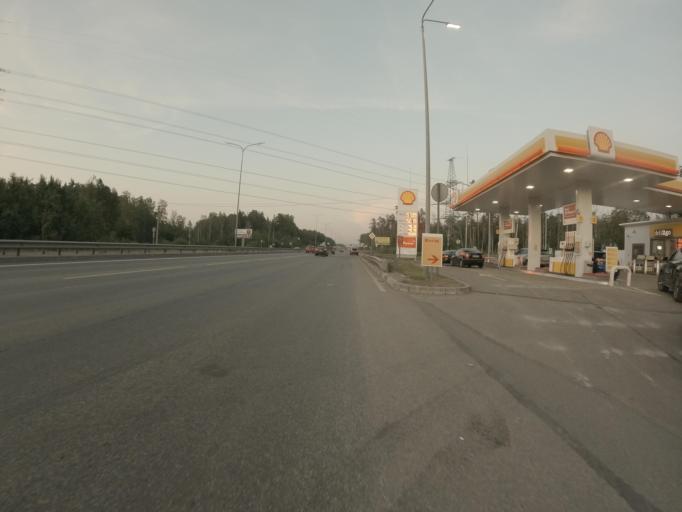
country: RU
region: St.-Petersburg
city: Krasnogvargeisky
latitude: 59.9453
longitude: 30.5209
